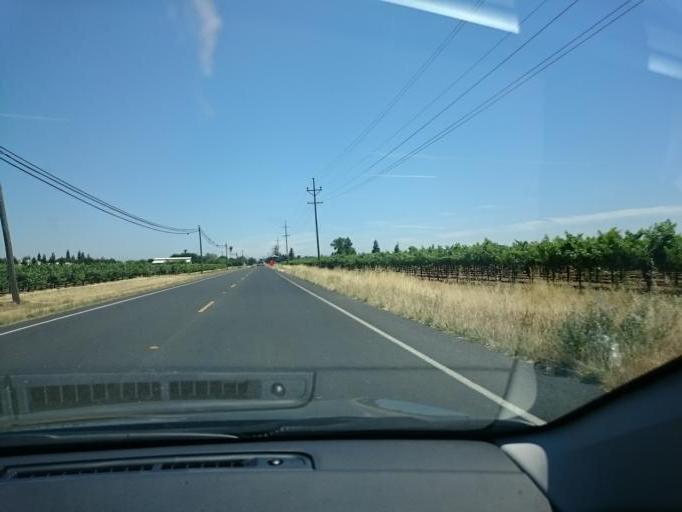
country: US
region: California
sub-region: San Joaquin County
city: Lockeford
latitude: 38.1897
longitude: -121.1966
